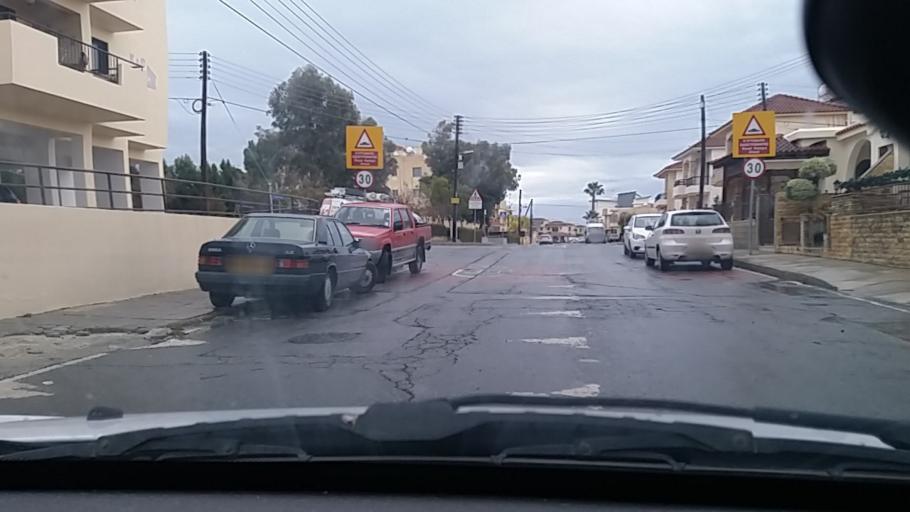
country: CY
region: Larnaka
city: Larnaca
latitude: 34.9360
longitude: 33.6262
